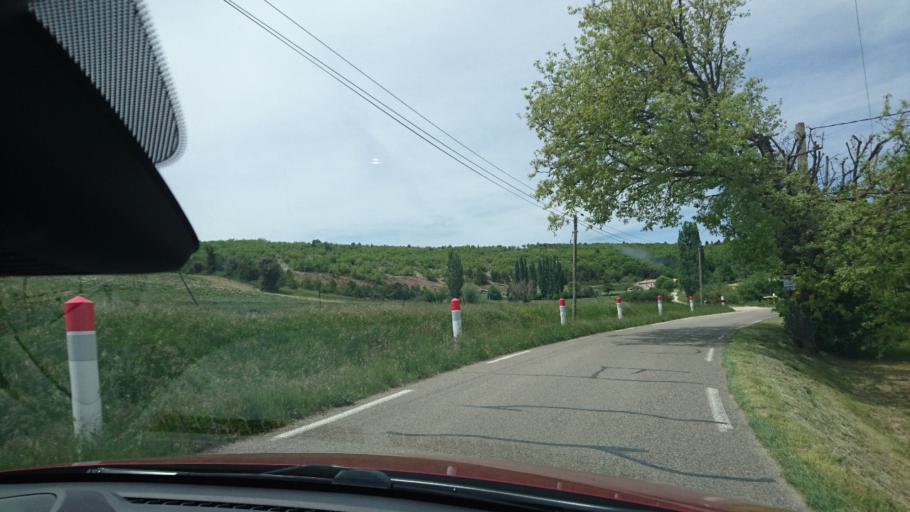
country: FR
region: Provence-Alpes-Cote d'Azur
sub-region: Departement du Vaucluse
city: Sault
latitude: 44.1043
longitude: 5.3997
